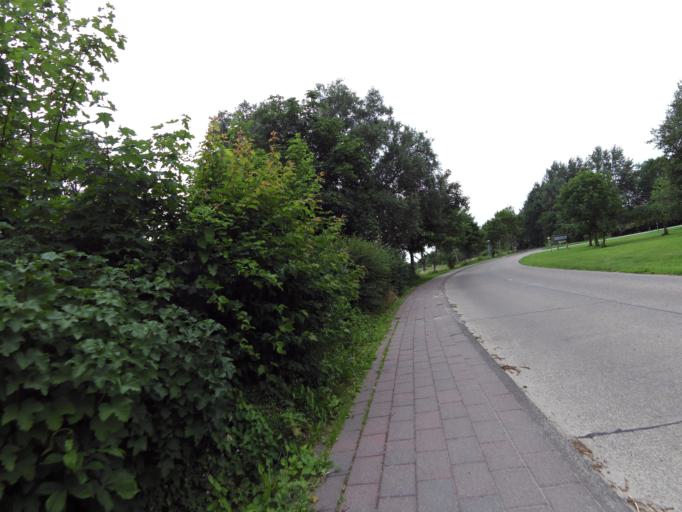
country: DE
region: Lower Saxony
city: Padingbuttel
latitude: 53.7280
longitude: 8.5315
